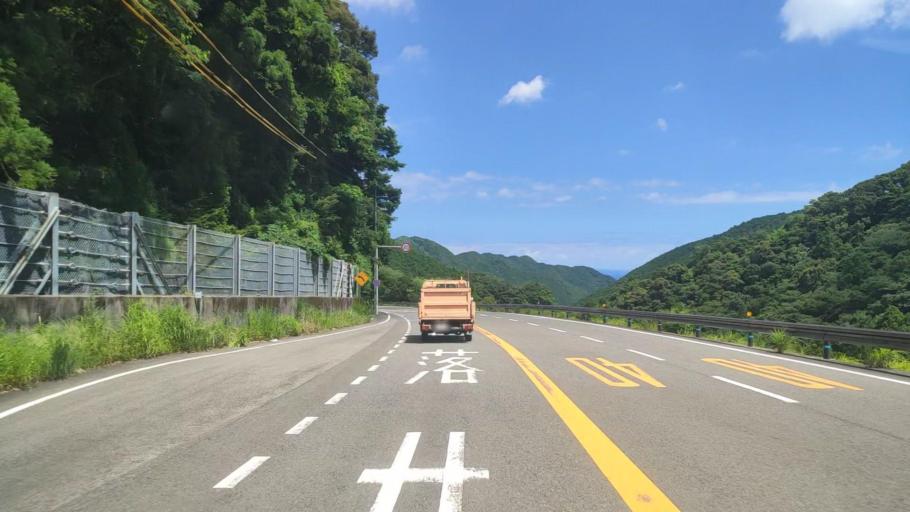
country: JP
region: Mie
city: Owase
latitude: 33.9215
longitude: 136.0977
